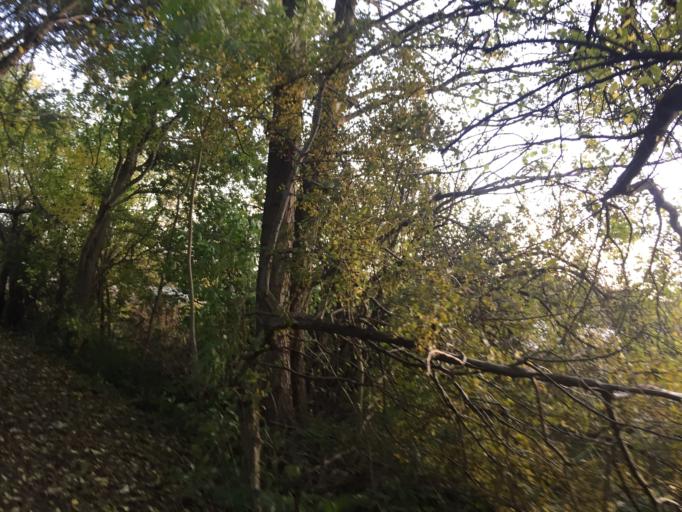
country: DK
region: Zealand
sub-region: Ringsted Kommune
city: Ringsted
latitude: 55.4838
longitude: 11.8098
